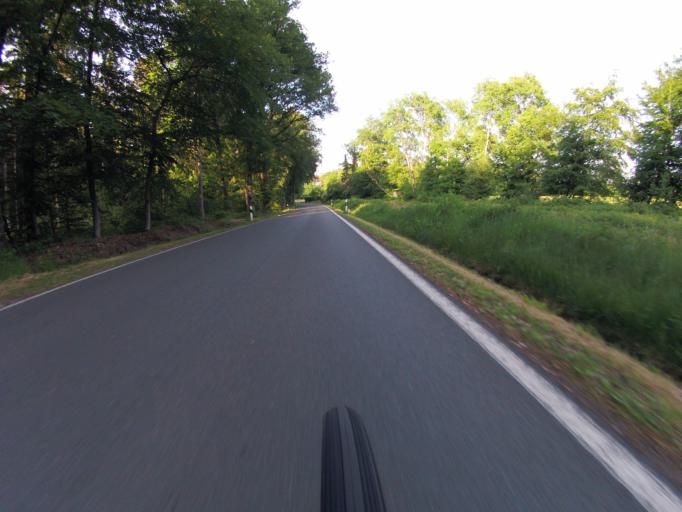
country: DE
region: North Rhine-Westphalia
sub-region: Regierungsbezirk Munster
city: Birgte
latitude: 52.2681
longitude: 7.6775
